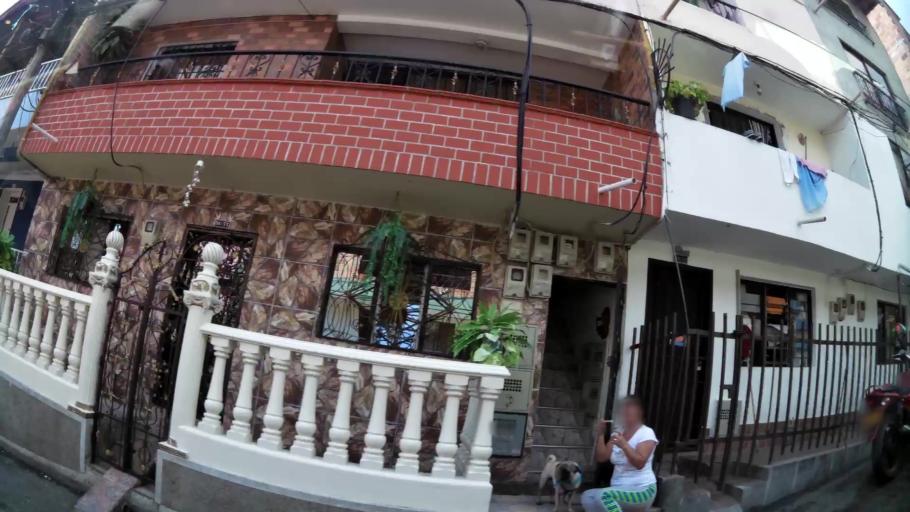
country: CO
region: Antioquia
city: Medellin
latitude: 6.2890
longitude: -75.5826
